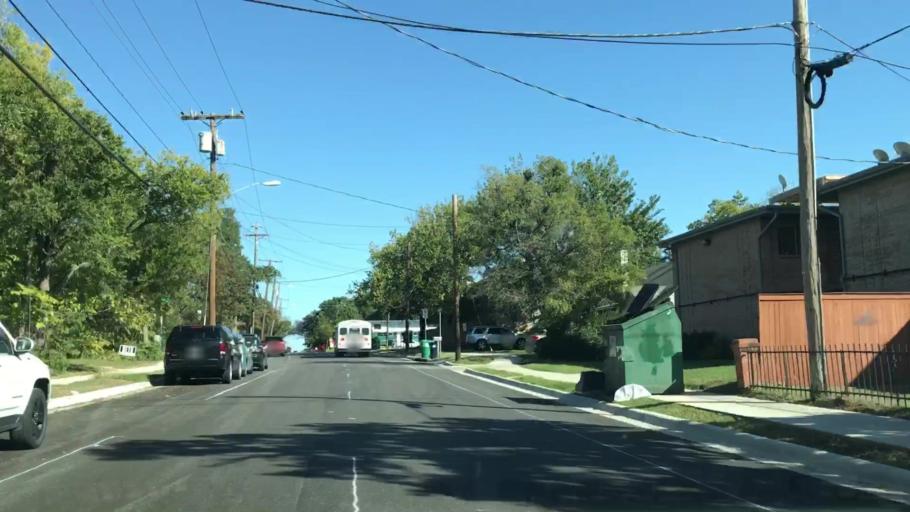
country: US
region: Texas
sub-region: Denton County
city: Denton
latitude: 33.2147
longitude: -97.1542
